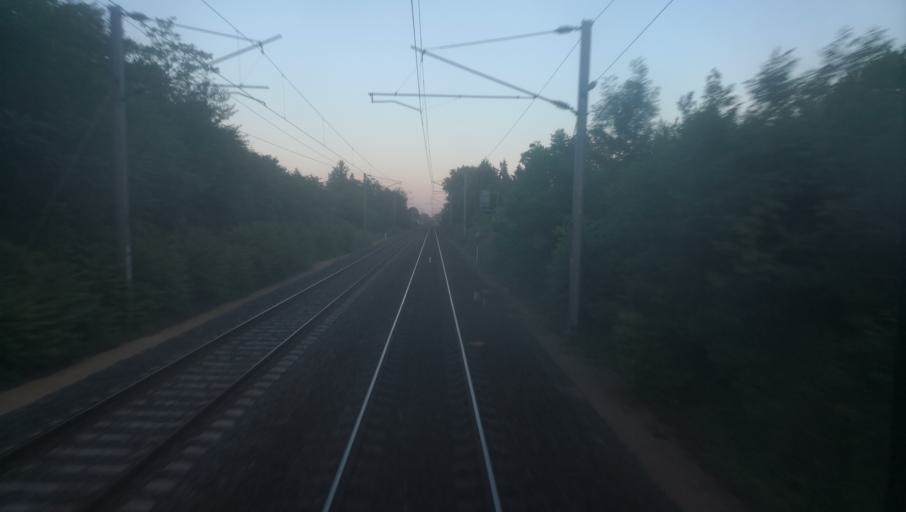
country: FR
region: Bourgogne
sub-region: Departement de la Nievre
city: Pouilly-sur-Loire
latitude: 47.2848
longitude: 2.9588
